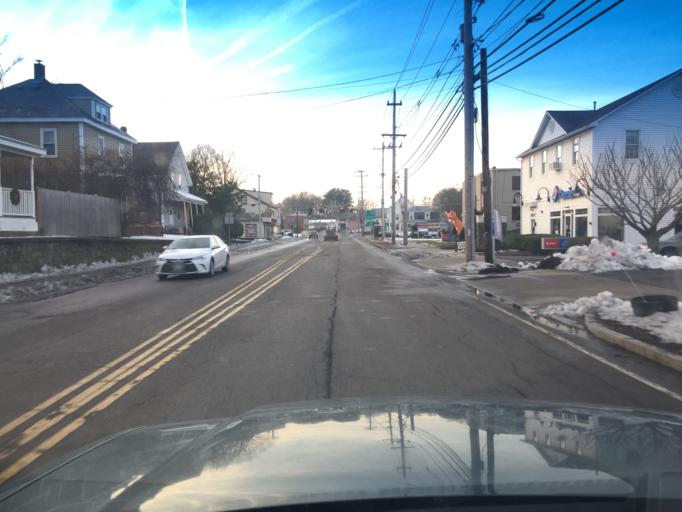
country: US
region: Massachusetts
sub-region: Norfolk County
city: Franklin
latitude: 42.0806
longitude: -71.3876
